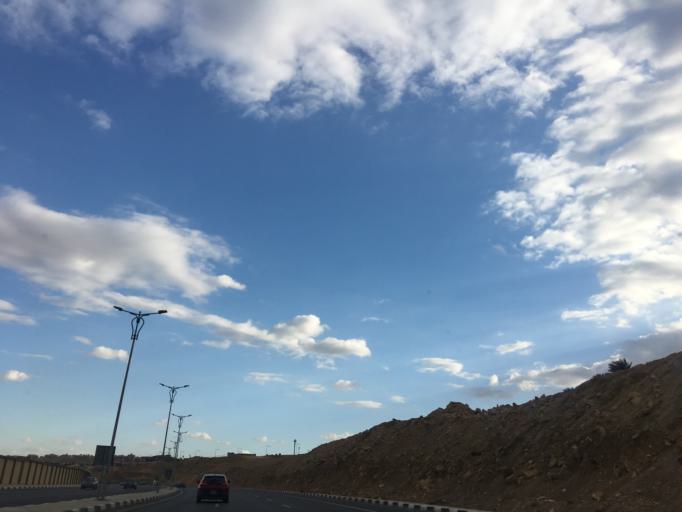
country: EG
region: Muhafazat al Qahirah
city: Cairo
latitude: 30.0309
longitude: 31.3089
